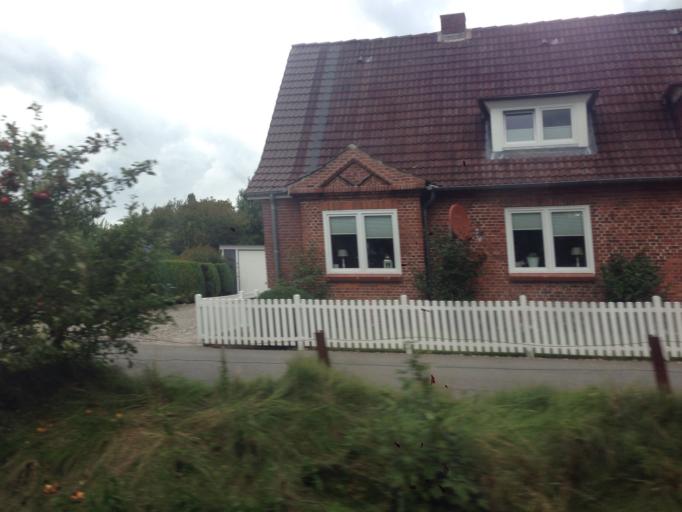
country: DE
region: Schleswig-Holstein
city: Niebull
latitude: 54.7962
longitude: 8.8321
